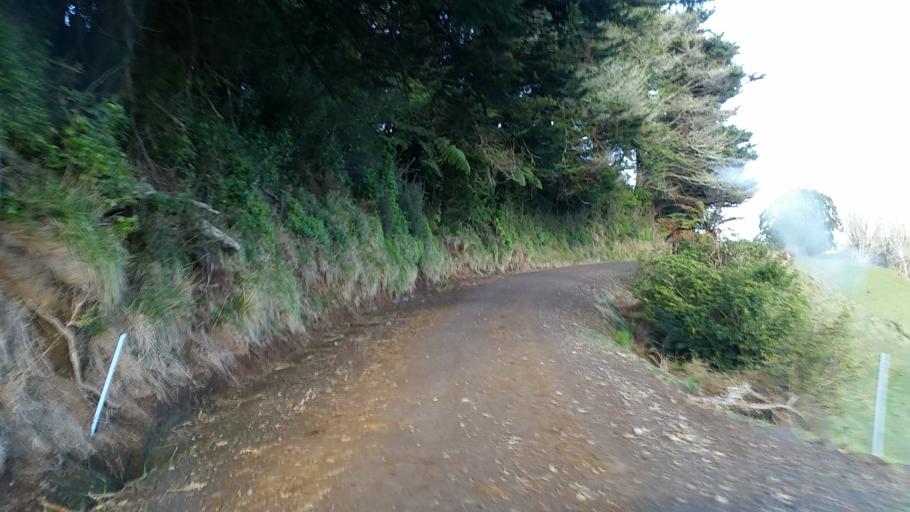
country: NZ
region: Taranaki
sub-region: South Taranaki District
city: Eltham
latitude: -39.2444
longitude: 174.3829
